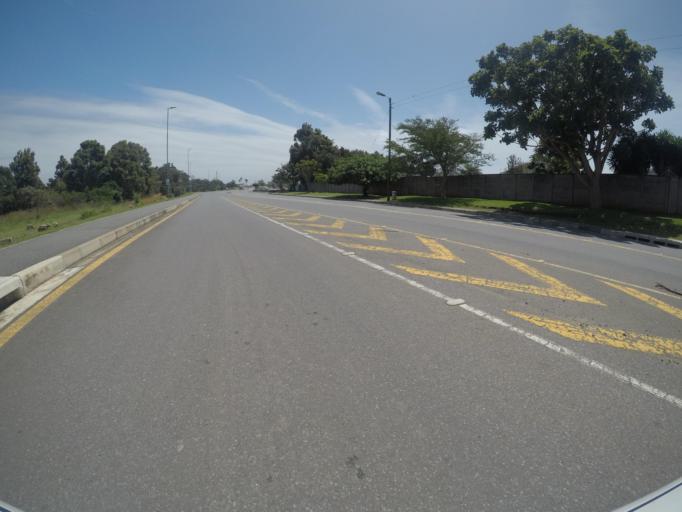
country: ZA
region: Eastern Cape
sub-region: Buffalo City Metropolitan Municipality
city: East London
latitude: -32.9382
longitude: 27.9936
